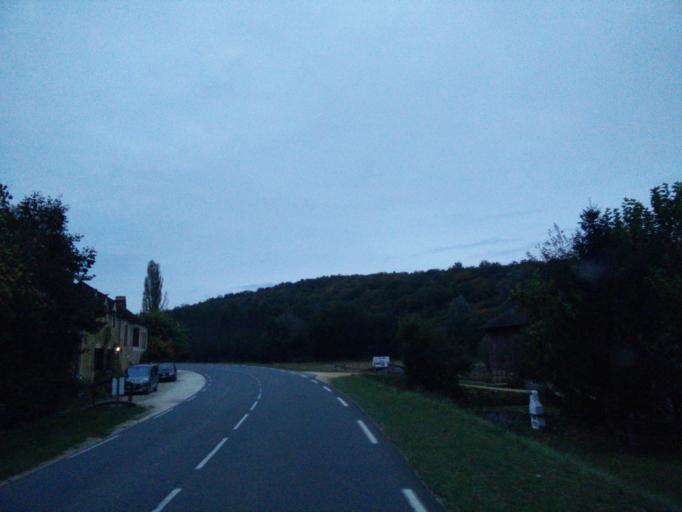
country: FR
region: Aquitaine
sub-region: Departement de la Dordogne
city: Saint-Cyprien
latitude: 44.9154
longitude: 1.1082
